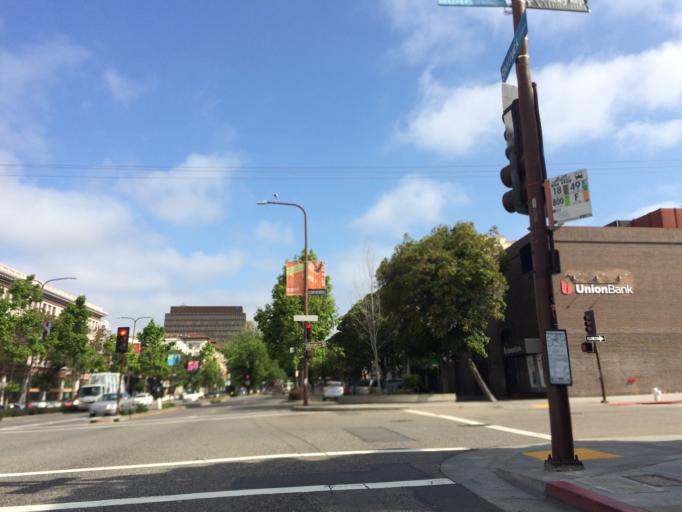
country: US
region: California
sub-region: Alameda County
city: Berkeley
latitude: 37.8666
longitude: -122.2676
